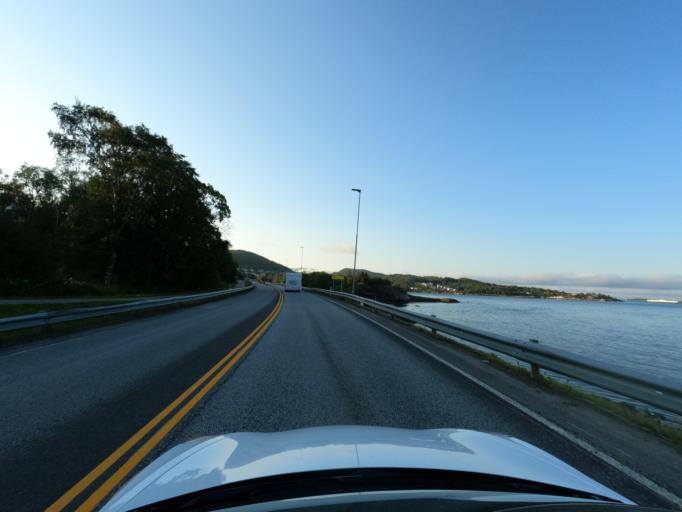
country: NO
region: Troms
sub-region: Harstad
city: Harstad
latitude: 68.7641
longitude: 16.5606
